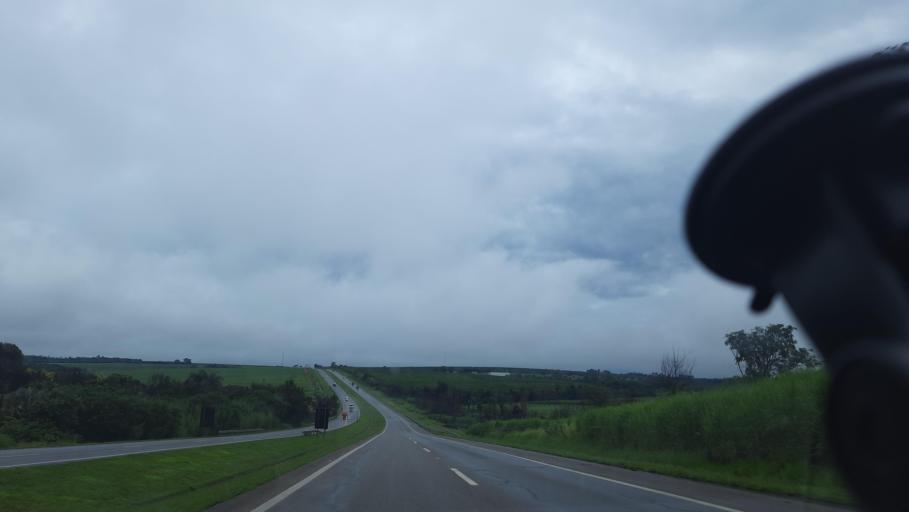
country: BR
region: Sao Paulo
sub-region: Aguai
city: Aguai
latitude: -22.1202
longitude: -47.0018
